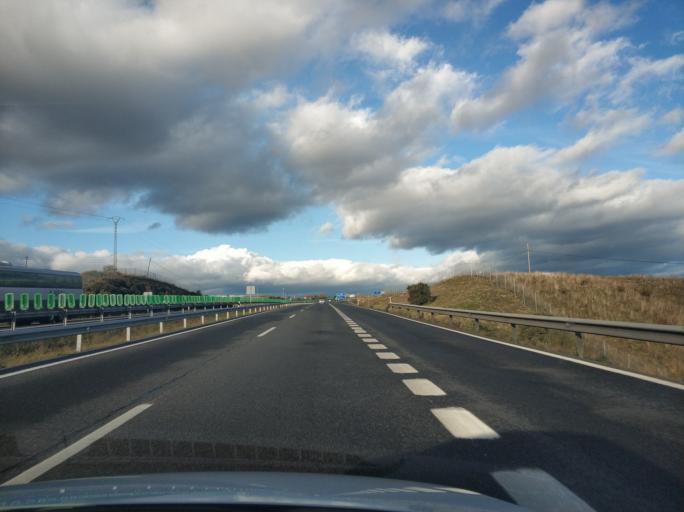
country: ES
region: Madrid
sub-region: Provincia de Madrid
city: El Molar
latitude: 40.7071
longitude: -3.5828
